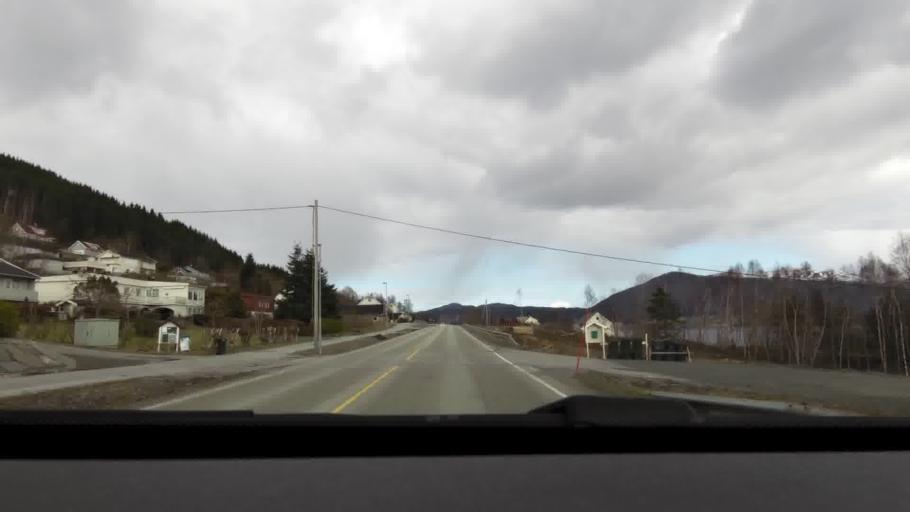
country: NO
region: More og Romsdal
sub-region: Kristiansund
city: Rensvik
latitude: 63.1097
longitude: 7.7757
